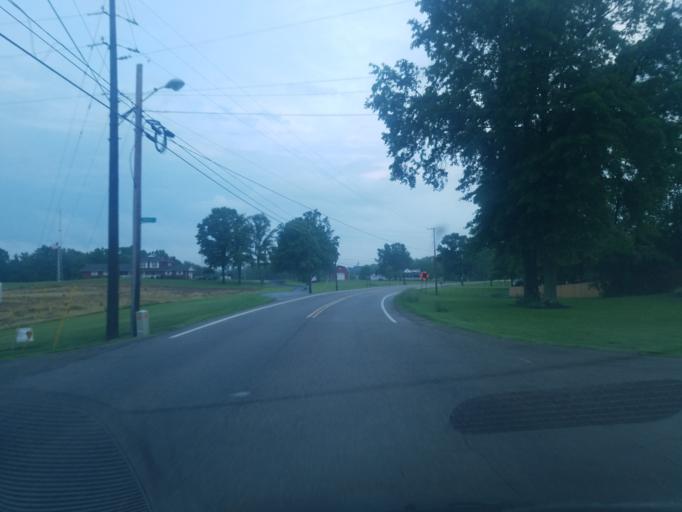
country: US
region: Ohio
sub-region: Columbiana County
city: Salem
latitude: 40.8642
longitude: -80.8860
